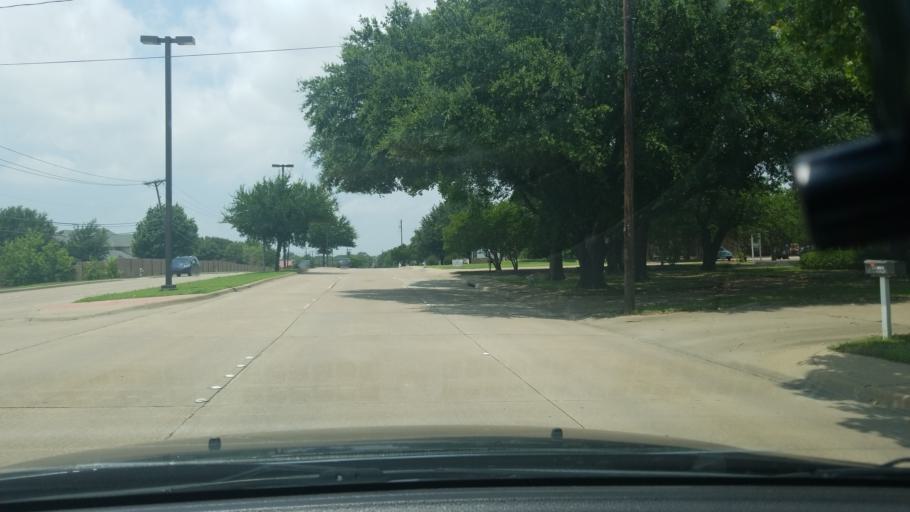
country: US
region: Texas
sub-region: Dallas County
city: Sunnyvale
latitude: 32.8141
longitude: -96.6003
